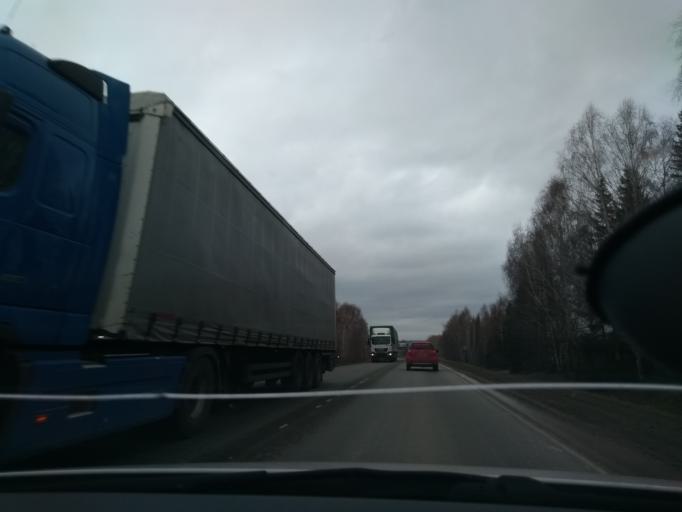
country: RU
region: Perm
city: Kukushtan
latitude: 57.4884
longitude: 56.6673
